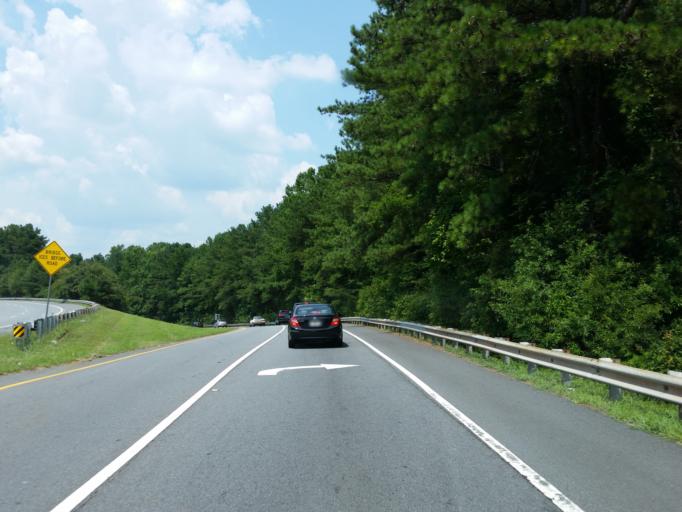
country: US
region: Georgia
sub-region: Cobb County
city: Marietta
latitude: 33.9581
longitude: -84.4961
